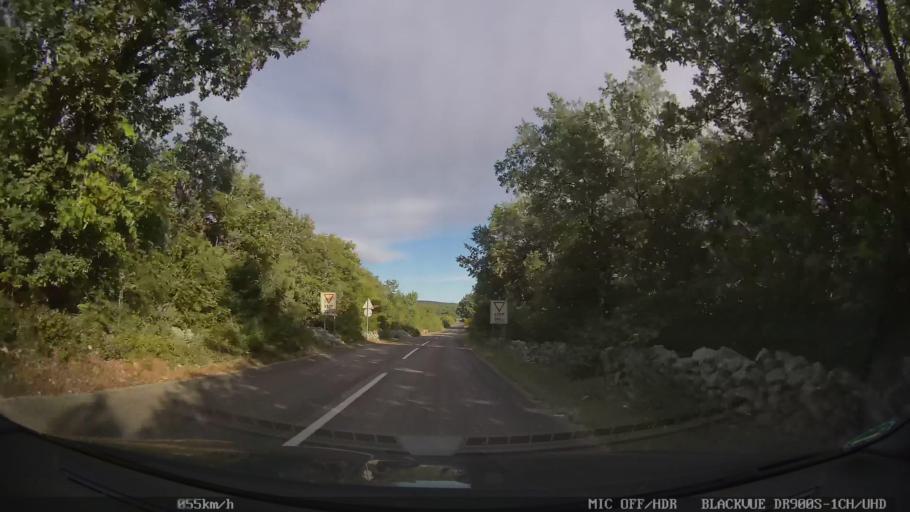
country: HR
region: Primorsko-Goranska
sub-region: Grad Krk
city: Krk
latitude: 45.0594
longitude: 14.4827
